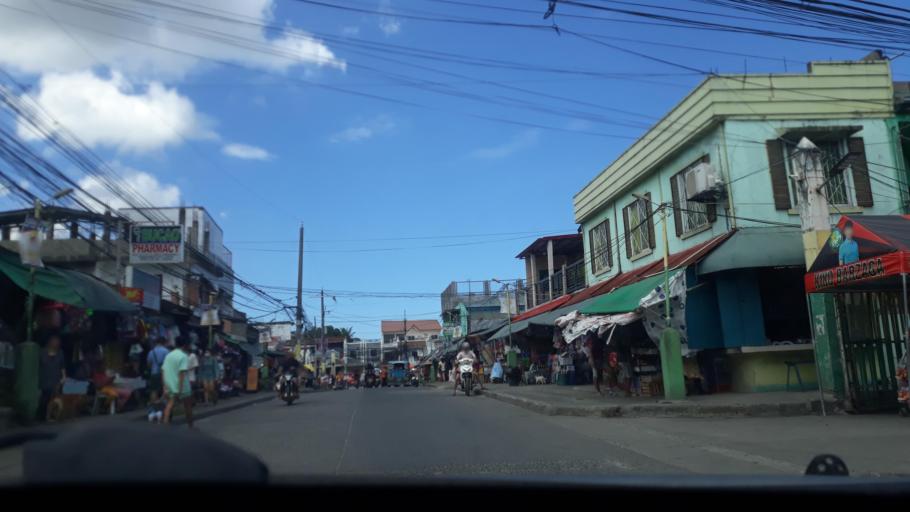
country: PH
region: Calabarzon
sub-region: Province of Cavite
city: Dasmarinas
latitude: 14.3154
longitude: 120.9591
